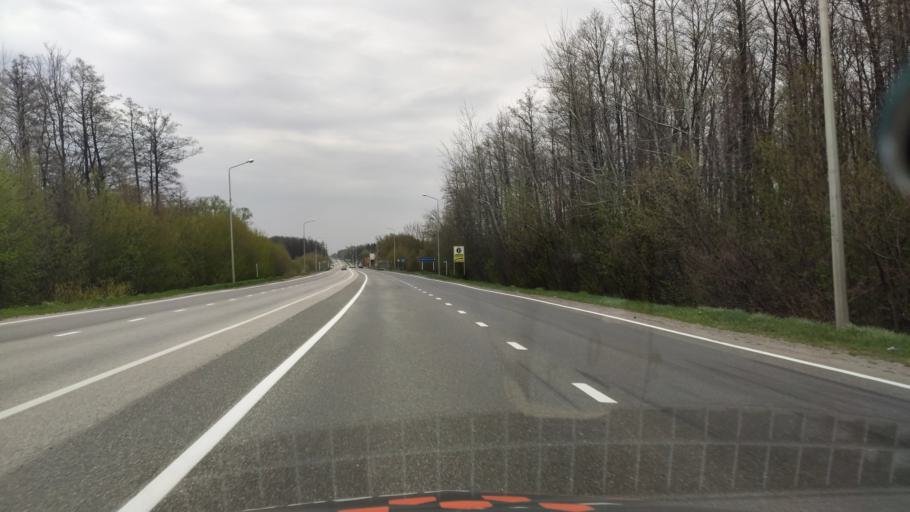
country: RU
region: Belgorod
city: Staryy Oskol
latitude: 51.3512
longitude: 37.8283
